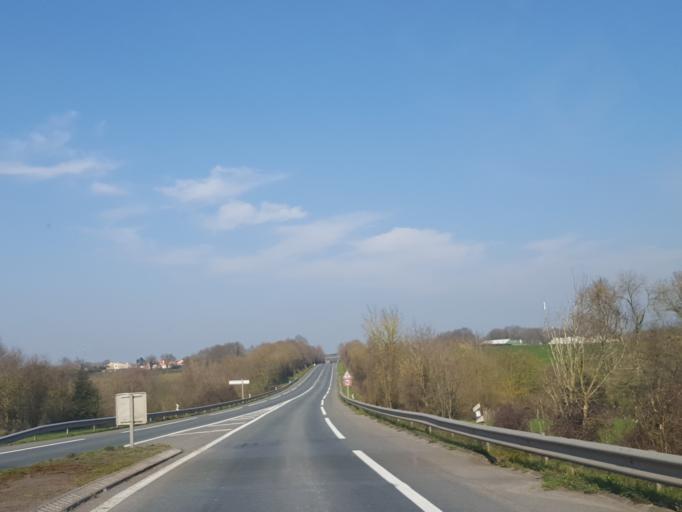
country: FR
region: Pays de la Loire
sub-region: Departement de la Vendee
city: Saint-Fulgent
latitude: 46.8376
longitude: -1.1618
